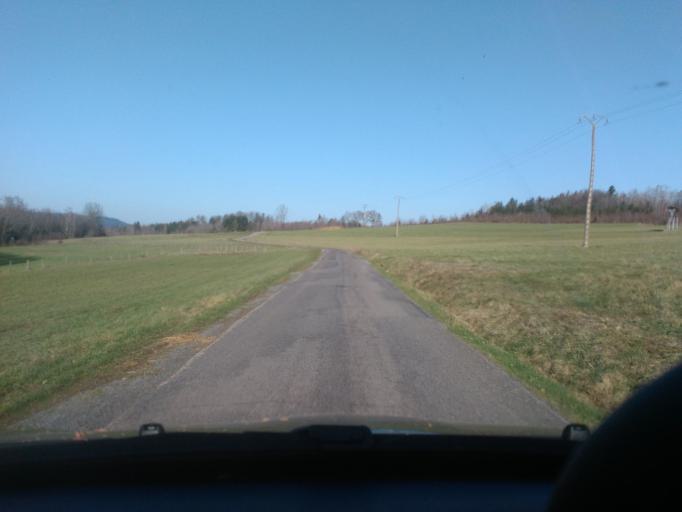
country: FR
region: Lorraine
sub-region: Departement des Vosges
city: Moyenmoutier
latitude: 48.3597
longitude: 6.9216
